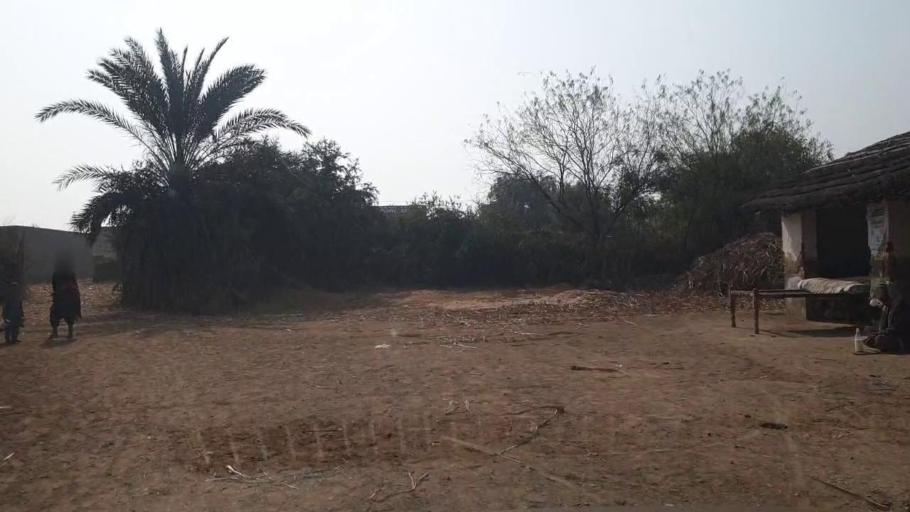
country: PK
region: Sindh
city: Hala
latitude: 25.9729
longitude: 68.4317
